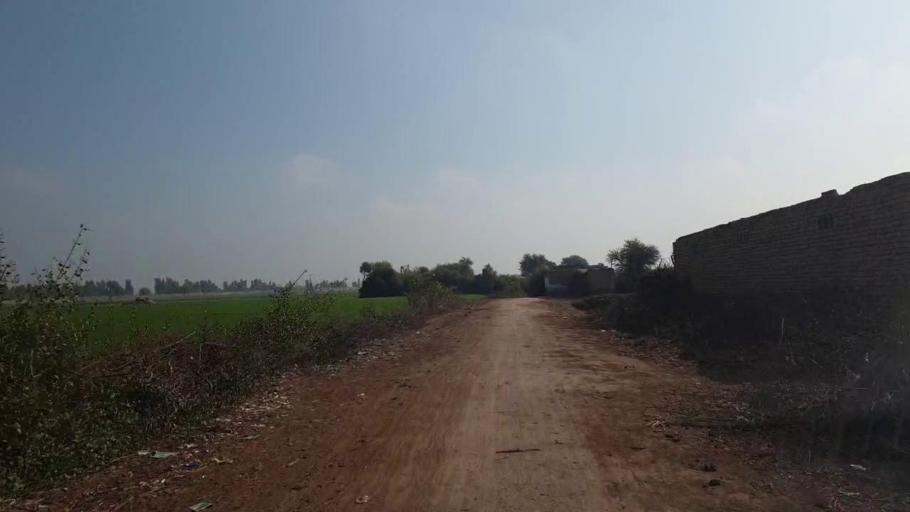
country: PK
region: Sindh
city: Shahdadpur
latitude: 26.0048
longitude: 68.5911
